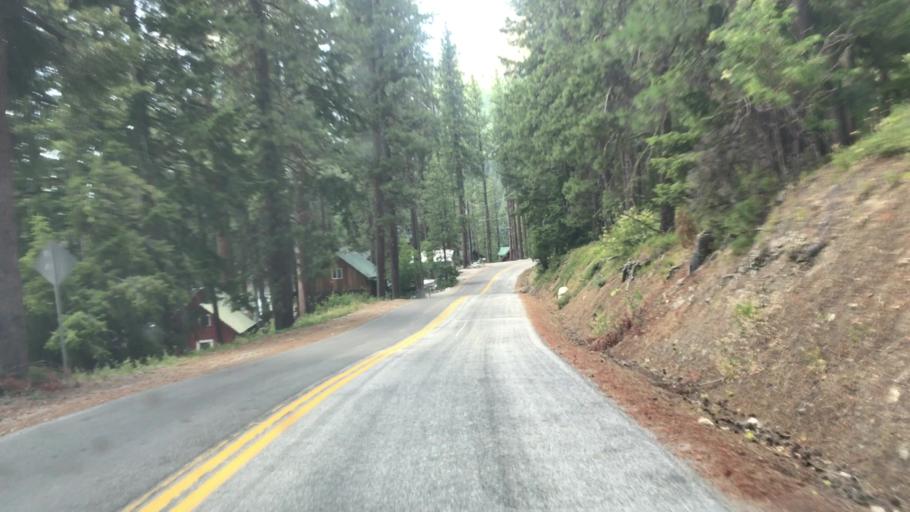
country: US
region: Washington
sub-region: Chelan County
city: Leavenworth
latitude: 47.8313
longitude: -120.7806
